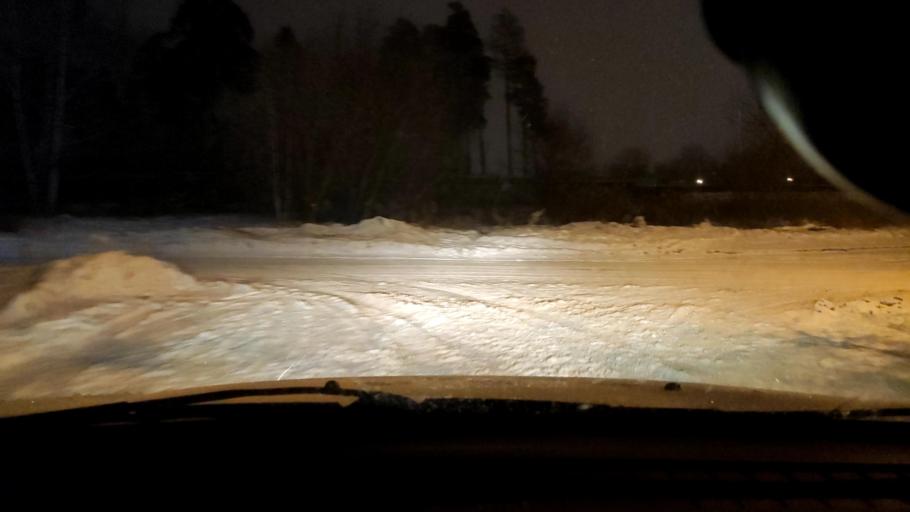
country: RU
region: Perm
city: Overyata
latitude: 58.0085
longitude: 55.9416
